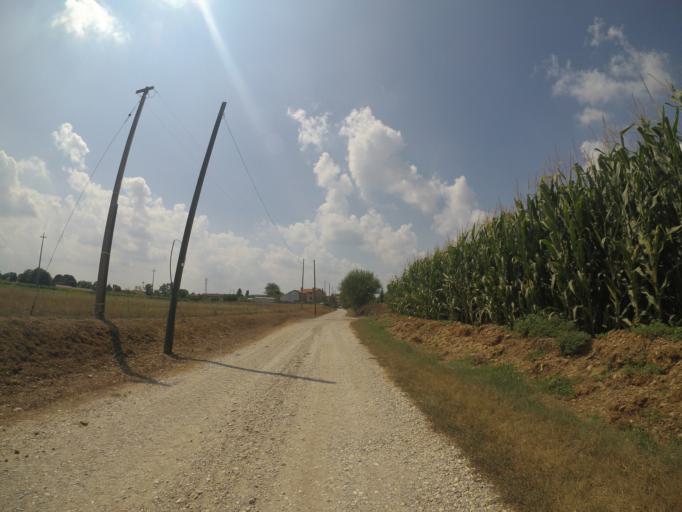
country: IT
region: Friuli Venezia Giulia
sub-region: Provincia di Udine
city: Bertiolo
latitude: 45.9477
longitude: 13.0256
